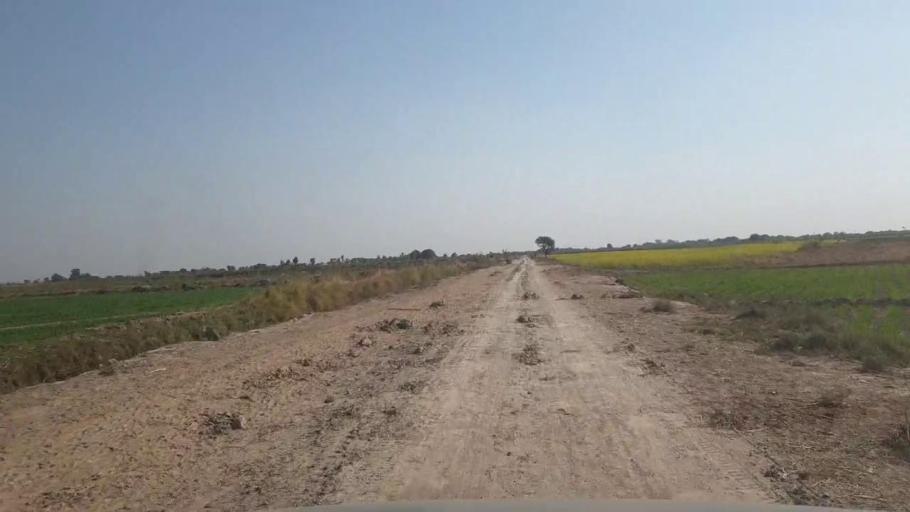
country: PK
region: Sindh
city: Chambar
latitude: 25.3194
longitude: 68.8705
